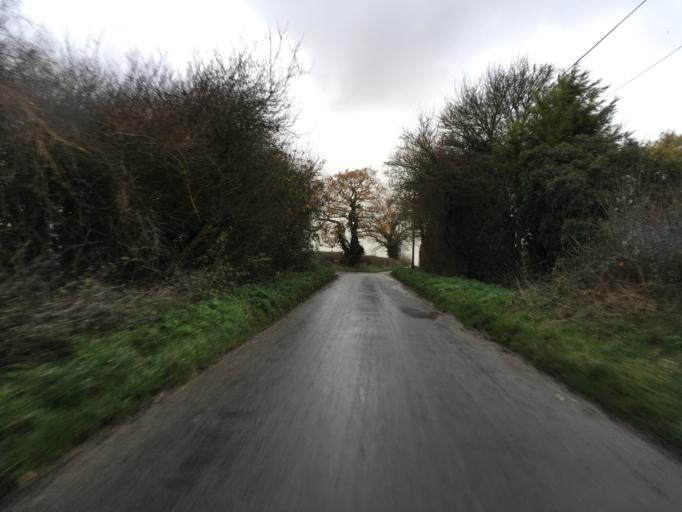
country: GB
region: England
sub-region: Wiltshire
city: Nettleton
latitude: 51.5107
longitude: -2.2639
